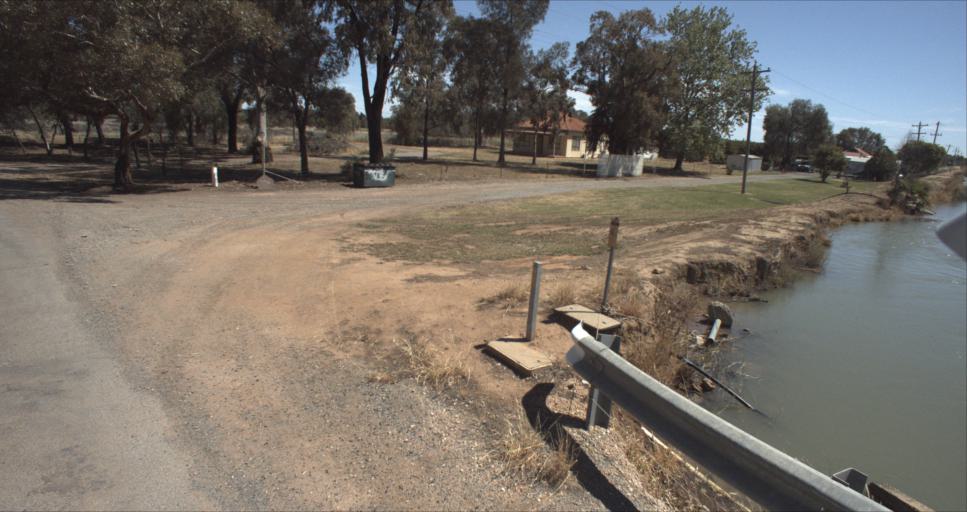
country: AU
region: New South Wales
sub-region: Leeton
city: Leeton
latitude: -34.5244
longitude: 146.3458
